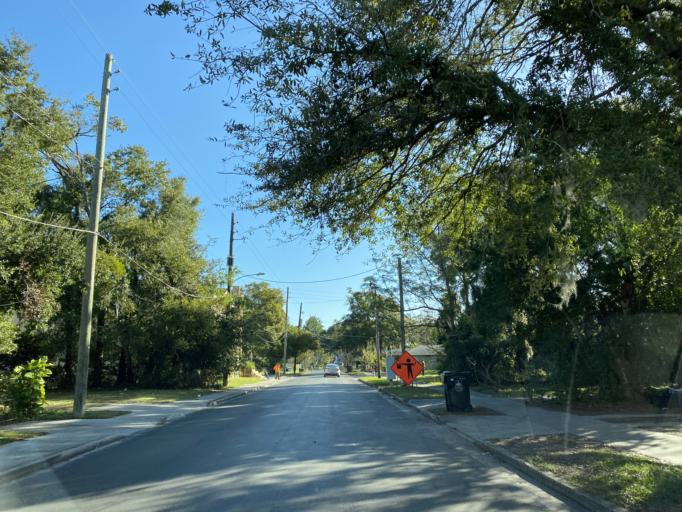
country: US
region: Florida
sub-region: Orange County
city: Orlando
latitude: 28.5467
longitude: -81.3929
